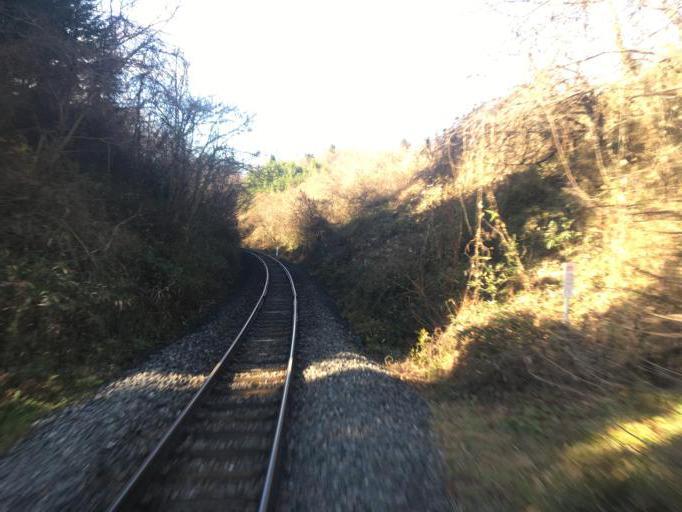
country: JP
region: Iwate
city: Ichinoseki
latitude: 38.9941
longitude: 141.2934
